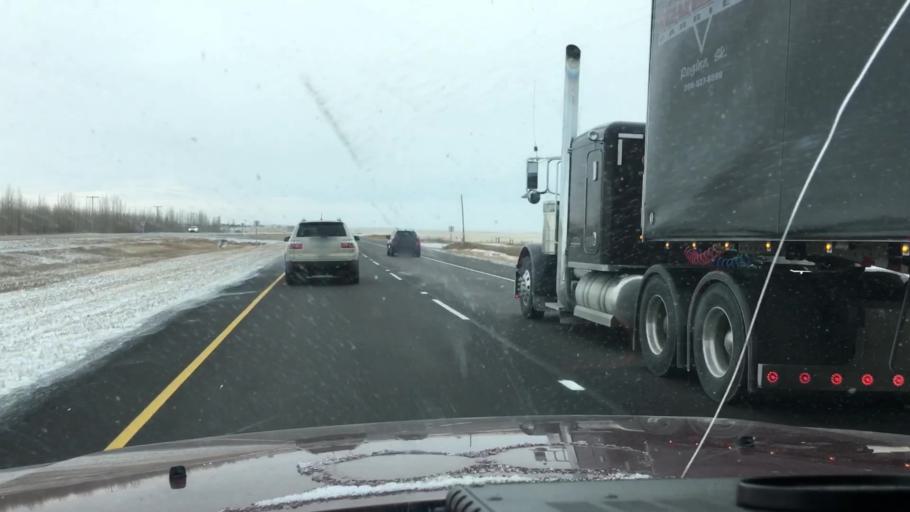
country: CA
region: Saskatchewan
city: Saskatoon
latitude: 51.7711
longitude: -106.4763
